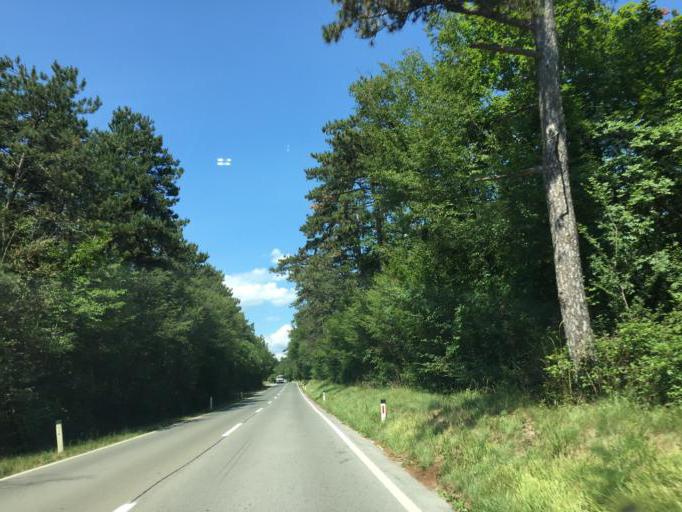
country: SI
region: Sezana
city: Sezana
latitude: 45.7313
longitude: 13.8673
